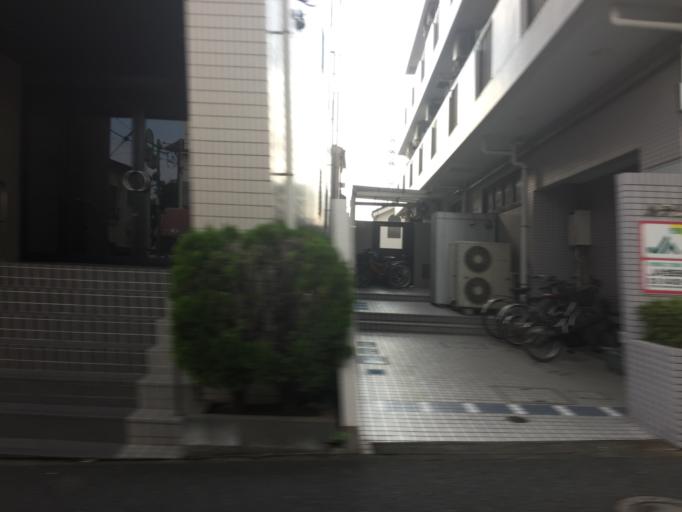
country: JP
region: Tokyo
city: Tokyo
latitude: 35.6112
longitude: 139.6477
